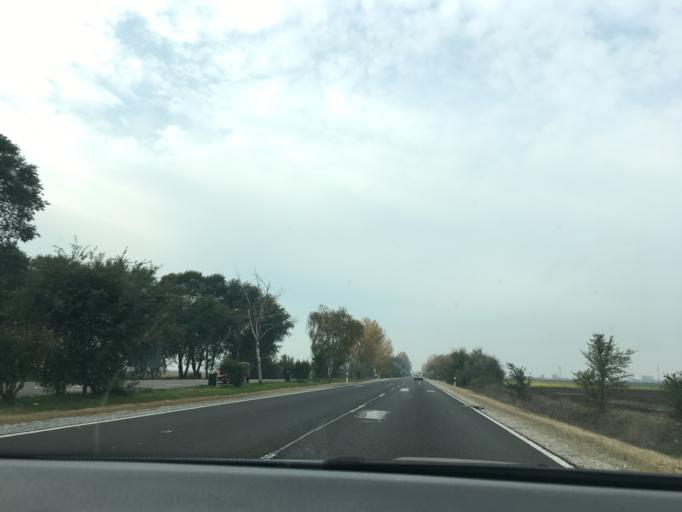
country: HU
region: Jasz-Nagykun-Szolnok
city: Toszeg
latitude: 47.1555
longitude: 20.1220
